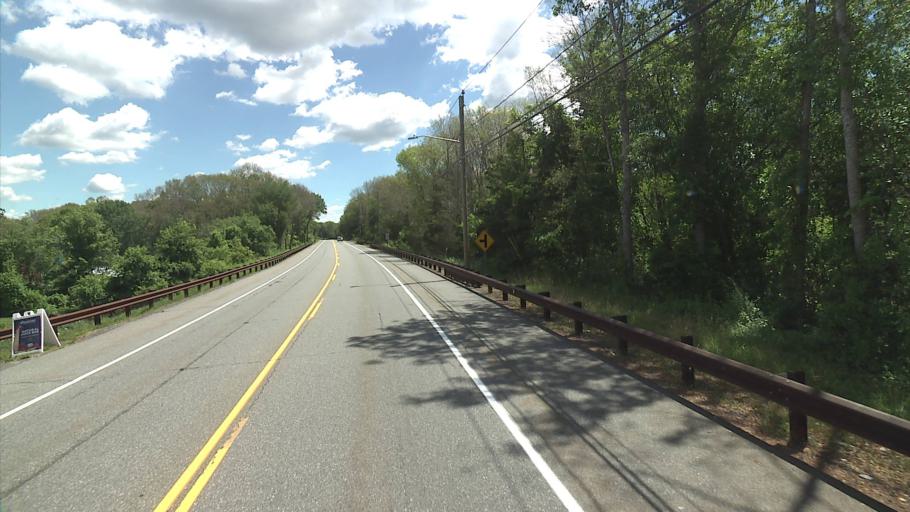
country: US
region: Connecticut
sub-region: New London County
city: Old Mystic
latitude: 41.3894
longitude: -71.9701
